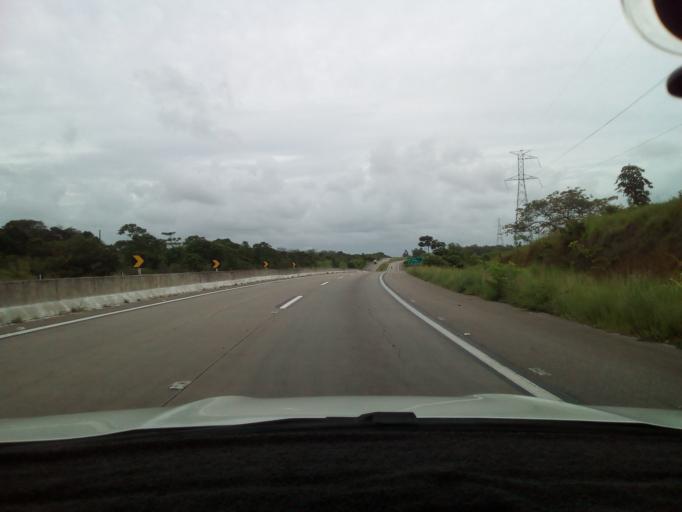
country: BR
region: Paraiba
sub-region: Conde
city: Conde
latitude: -7.3133
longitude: -34.9462
